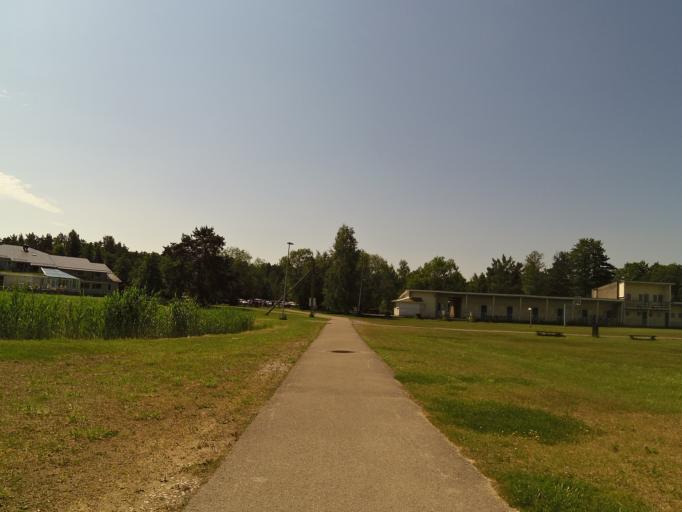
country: EE
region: Laeaene
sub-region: Haapsalu linn
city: Haapsalu
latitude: 58.9419
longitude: 23.5160
